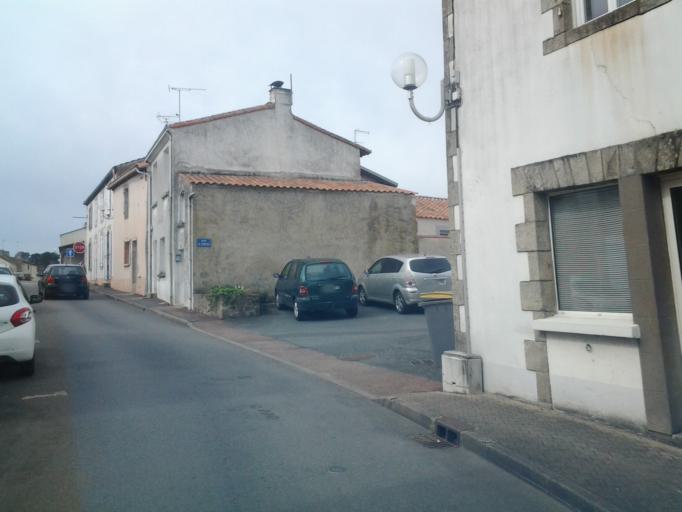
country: FR
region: Pays de la Loire
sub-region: Departement de la Vendee
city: Venansault
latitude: 46.6861
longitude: -1.5131
